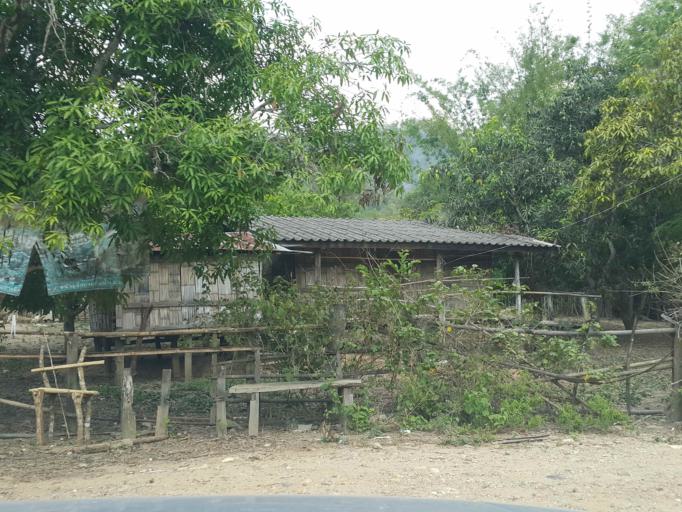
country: TH
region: Chiang Mai
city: Wiang Haeng
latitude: 19.4048
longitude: 98.7252
